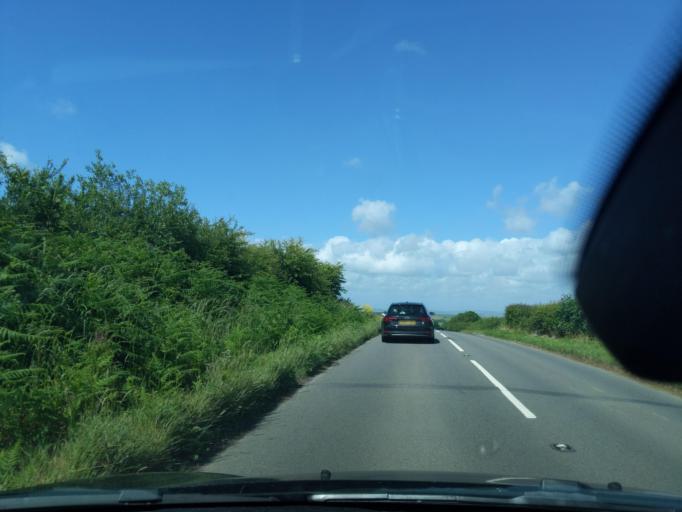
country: GB
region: England
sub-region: Devon
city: Fremington
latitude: 51.0118
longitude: -4.1091
